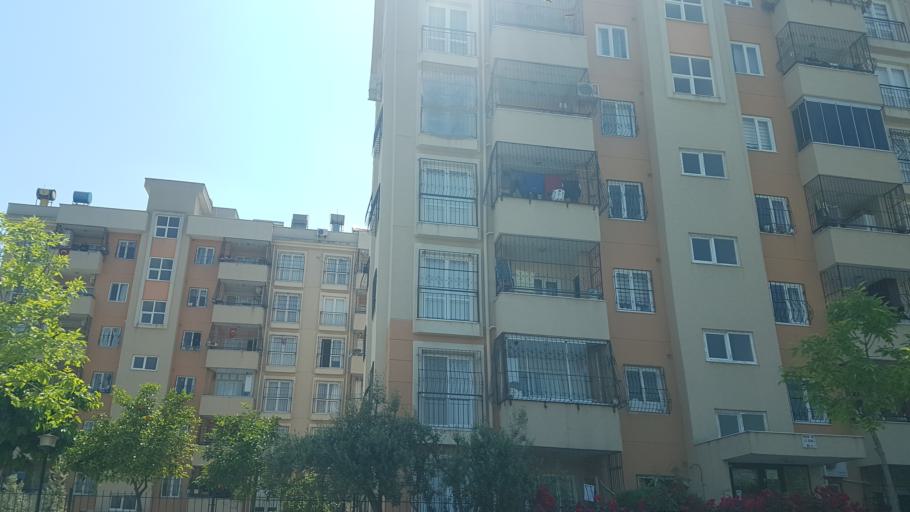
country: TR
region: Adana
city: Yuregir
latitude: 37.0195
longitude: 35.3731
